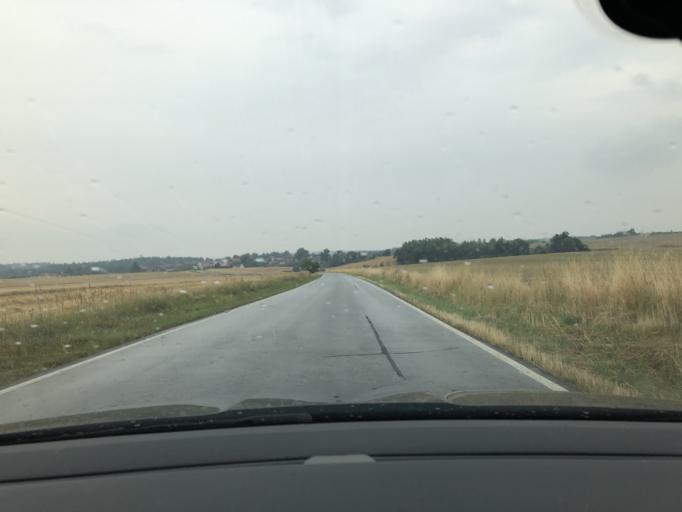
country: CZ
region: South Moravian
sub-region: Okres Znojmo
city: Jevisovice
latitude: 49.0293
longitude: 15.9643
